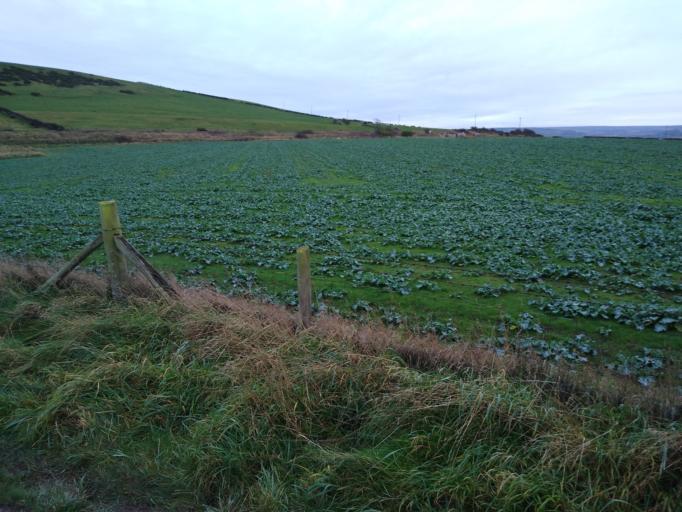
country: GB
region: England
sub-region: Redcar and Cleveland
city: Saltburn-by-the-Sea
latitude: 54.5868
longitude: -0.9354
